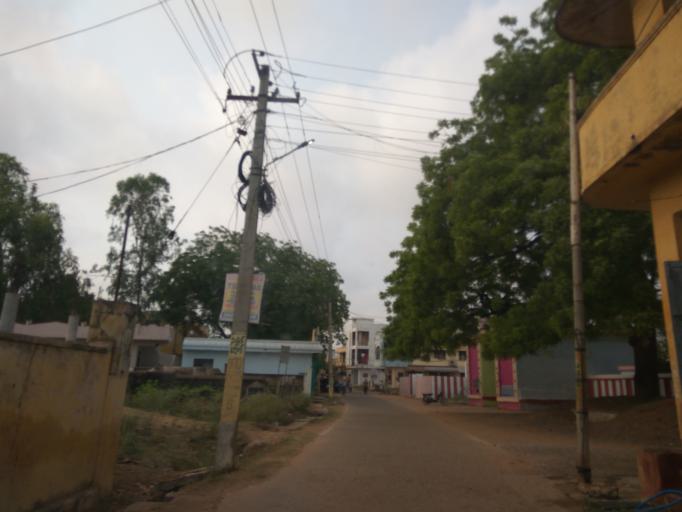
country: IN
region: Andhra Pradesh
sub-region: Prakasam
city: Kandukur
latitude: 15.2188
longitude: 79.9040
